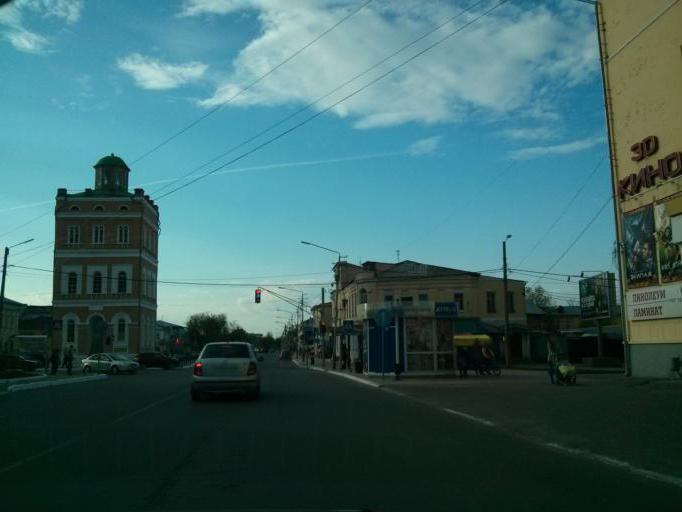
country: RU
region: Vladimir
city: Murom
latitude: 55.5775
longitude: 42.0537
